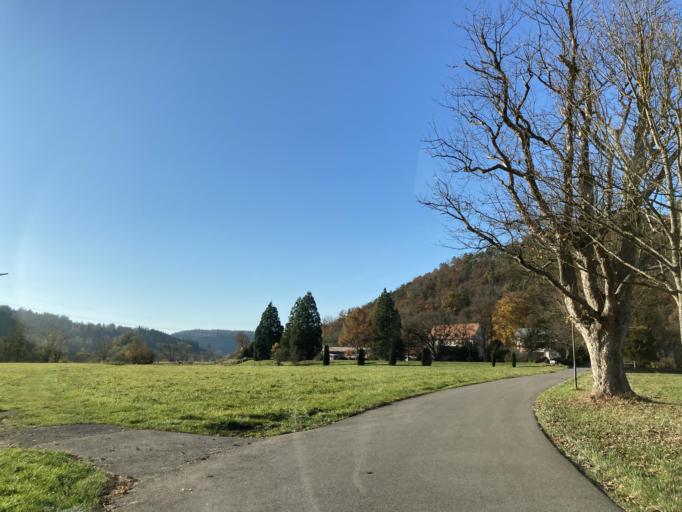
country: DE
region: Baden-Wuerttemberg
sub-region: Tuebingen Region
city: Rottenburg
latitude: 48.4594
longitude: 8.8995
